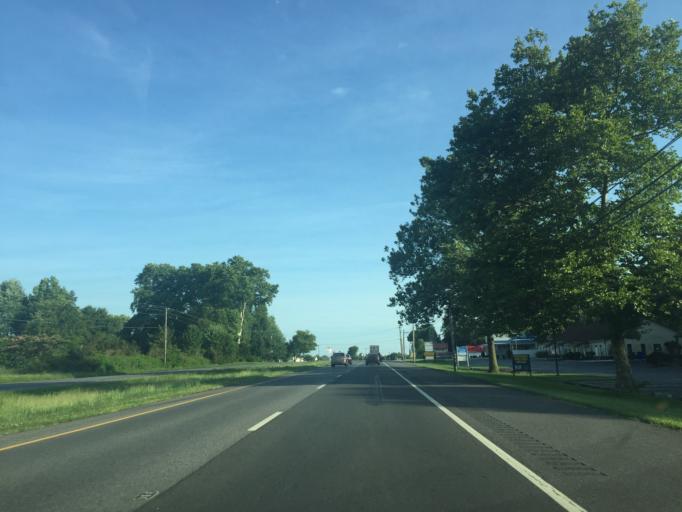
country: US
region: Delaware
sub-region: Kent County
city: Cheswold
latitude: 39.2574
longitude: -75.5864
